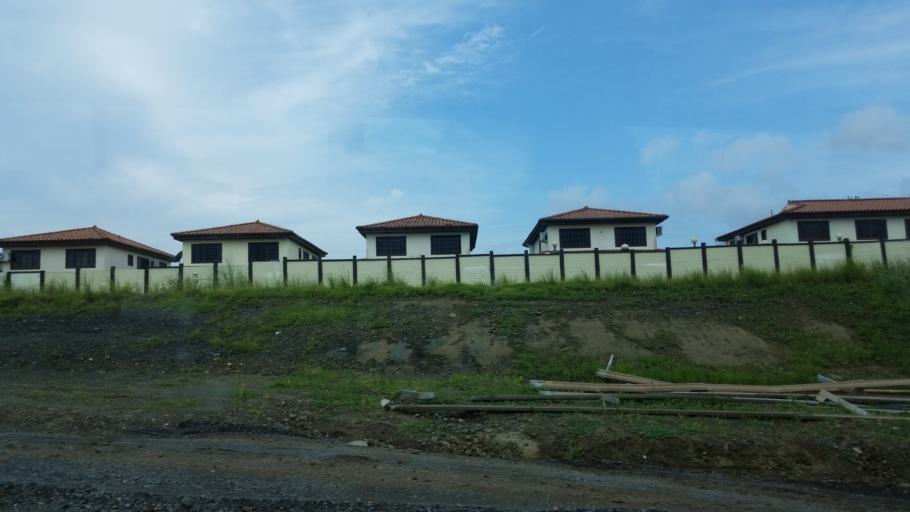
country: PA
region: Panama
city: Las Cumbres
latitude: 9.1023
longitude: -79.5219
